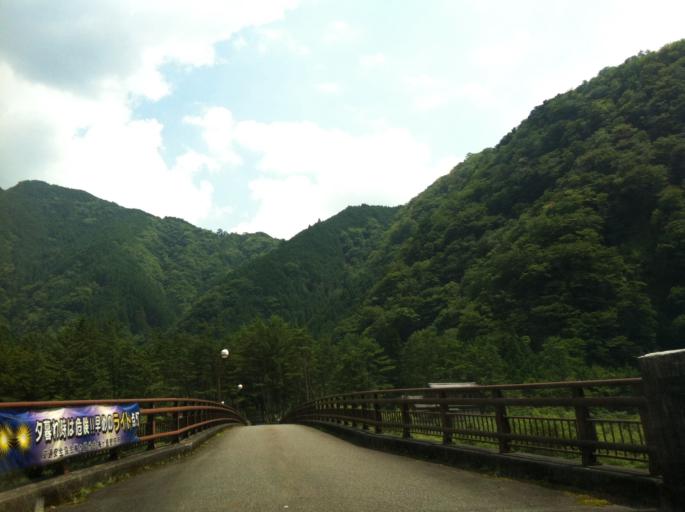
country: JP
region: Shizuoka
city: Fujinomiya
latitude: 35.2801
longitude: 138.3384
